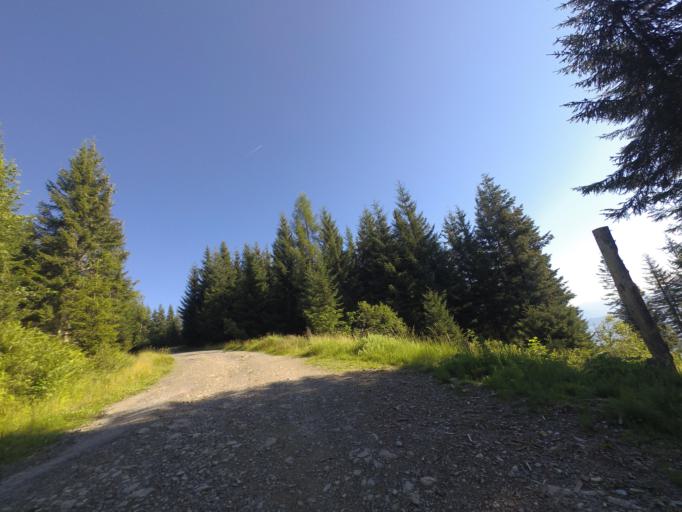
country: AT
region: Salzburg
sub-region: Politischer Bezirk Sankt Johann im Pongau
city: Sankt Veit im Pongau
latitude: 47.3446
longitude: 13.1609
